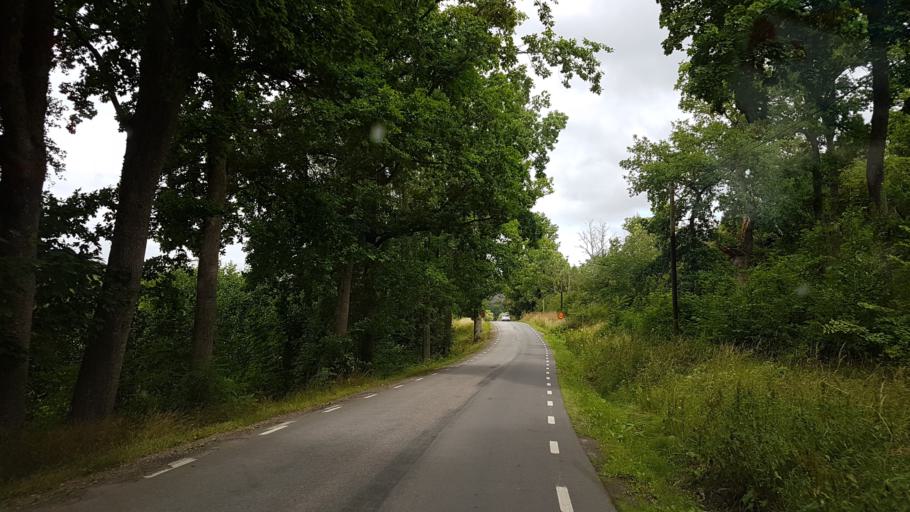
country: SE
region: OEstergoetland
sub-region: Valdemarsviks Kommun
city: Gusum
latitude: 58.4376
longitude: 16.5987
